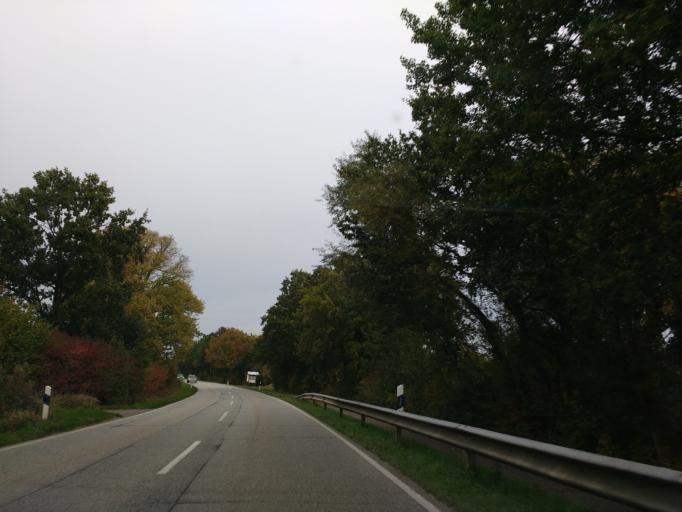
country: DE
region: Schleswig-Holstein
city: Gromitz
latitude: 54.1594
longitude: 10.9638
